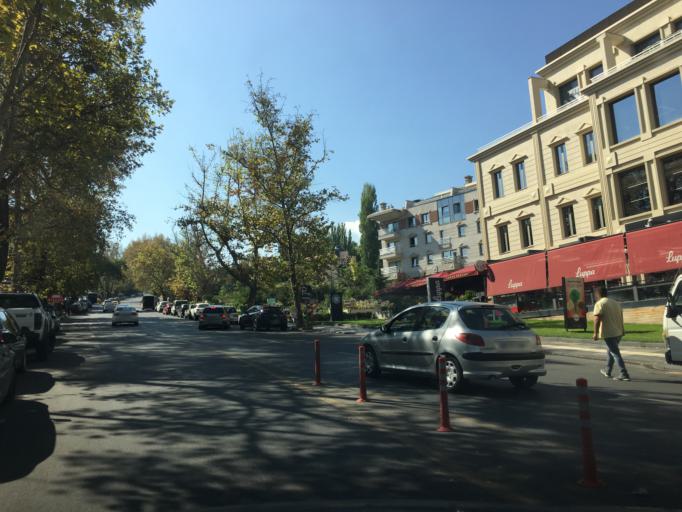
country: TR
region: Ankara
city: Cankaya
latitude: 39.8992
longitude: 32.8630
